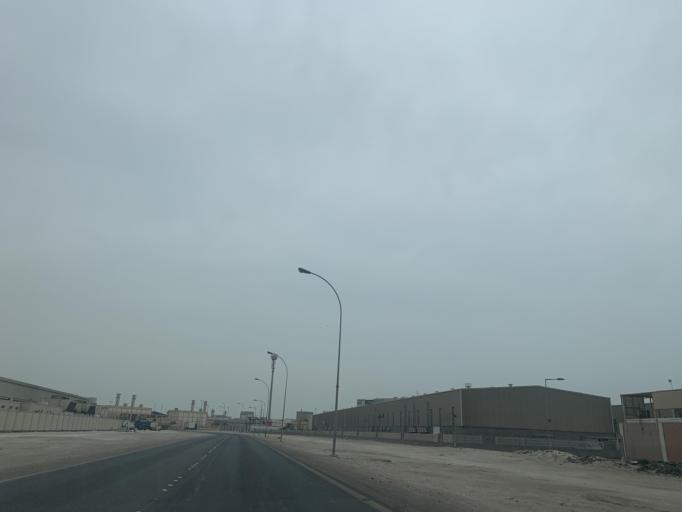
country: BH
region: Muharraq
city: Al Hadd
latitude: 26.2106
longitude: 50.6700
